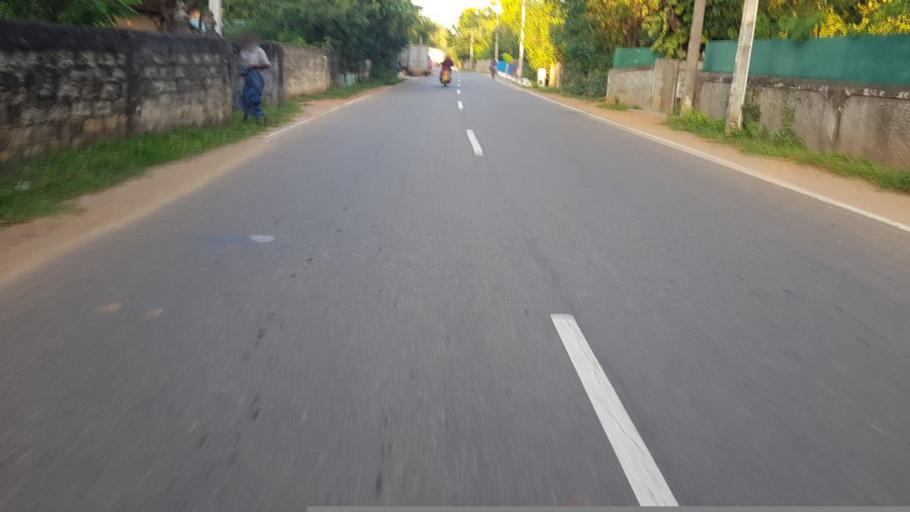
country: LK
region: Northern Province
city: Jaffna
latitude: 9.7332
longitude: 79.9515
